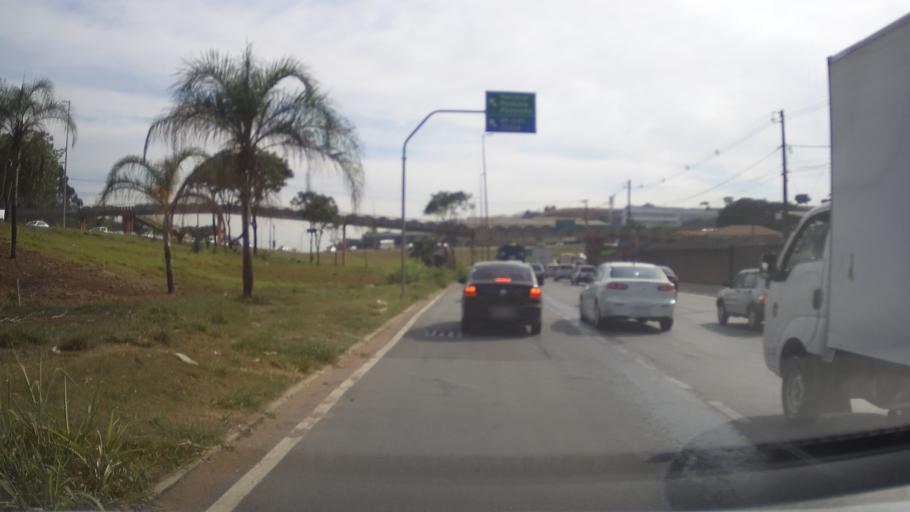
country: BR
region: Minas Gerais
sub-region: Contagem
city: Contagem
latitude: -19.9189
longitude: -44.0571
